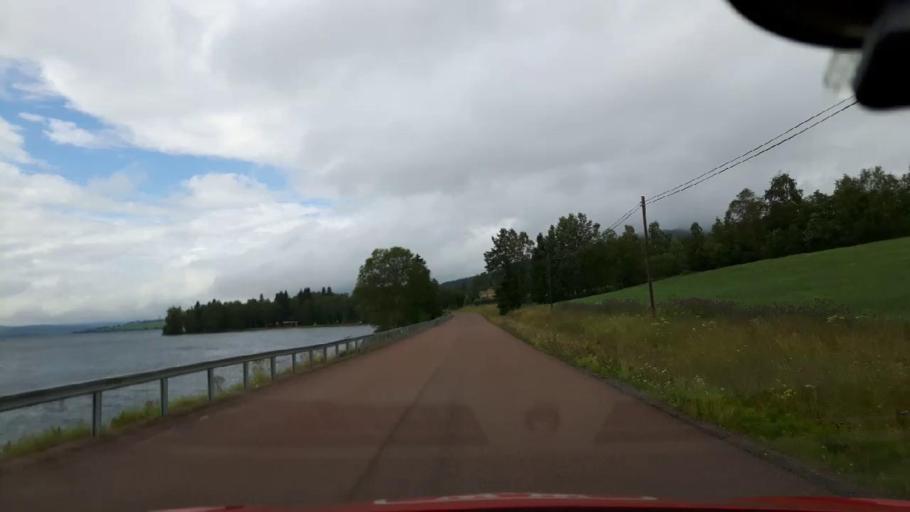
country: SE
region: Jaemtland
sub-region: Krokoms Kommun
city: Valla
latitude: 63.3736
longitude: 14.0269
